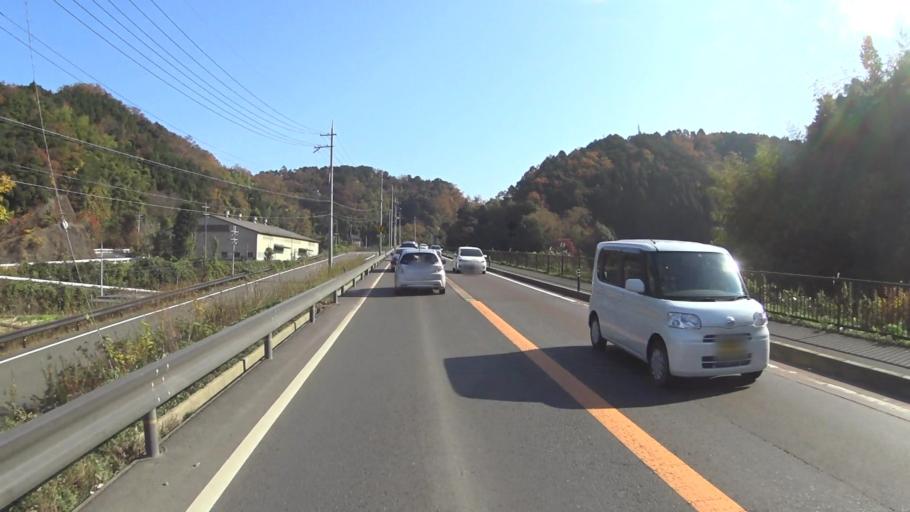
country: JP
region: Kyoto
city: Maizuru
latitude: 35.4499
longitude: 135.2712
